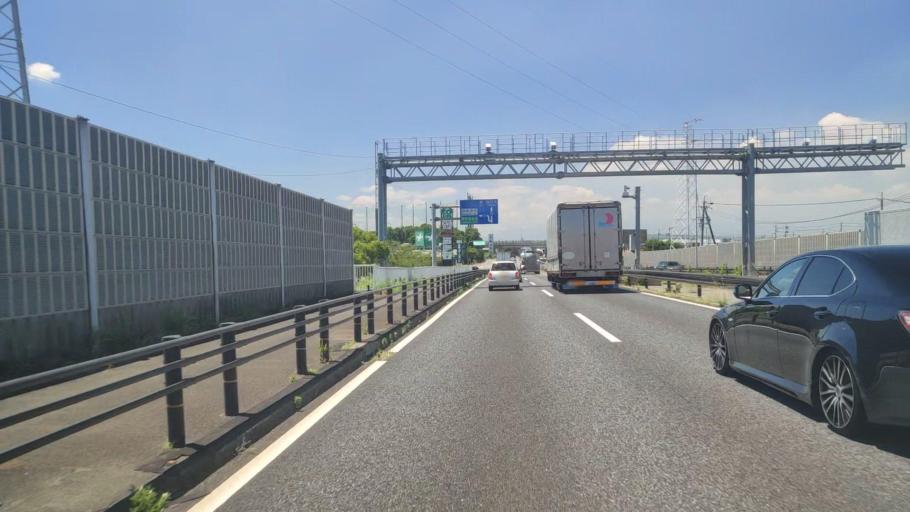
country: JP
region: Aichi
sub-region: Aisai-shi
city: Aisai
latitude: 35.0586
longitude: 136.7234
